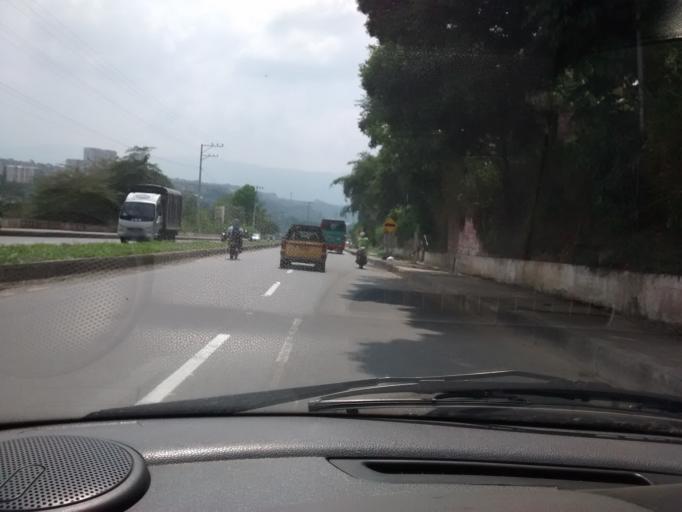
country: CO
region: Santander
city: Bucaramanga
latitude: 7.0952
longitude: -73.1176
